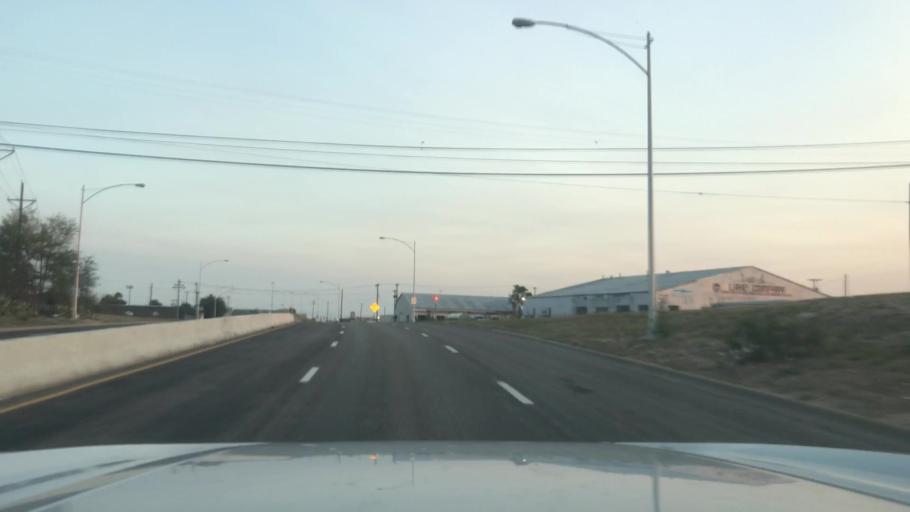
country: US
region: Texas
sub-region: Lubbock County
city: Lubbock
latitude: 33.6017
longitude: -101.8539
